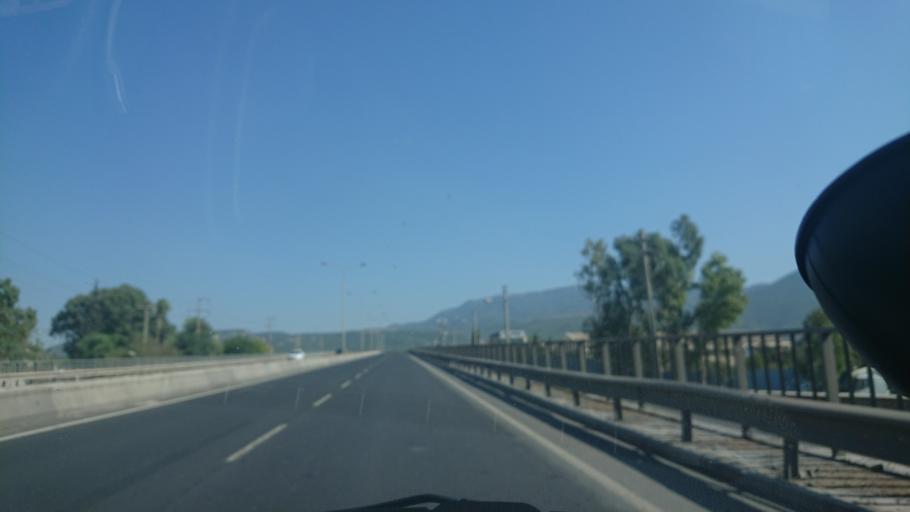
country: TR
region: Izmir
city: Bornova
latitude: 38.4535
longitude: 27.2627
